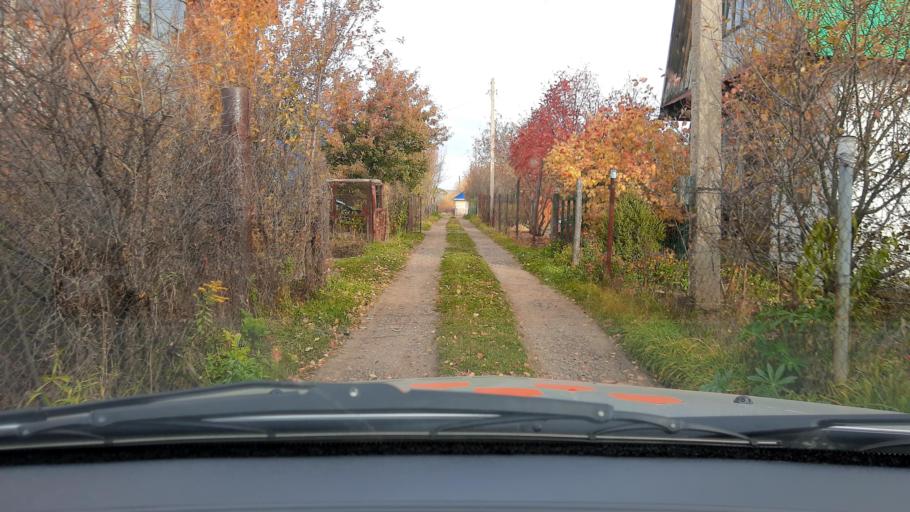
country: RU
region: Bashkortostan
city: Asanovo
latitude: 54.8053
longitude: 55.6124
